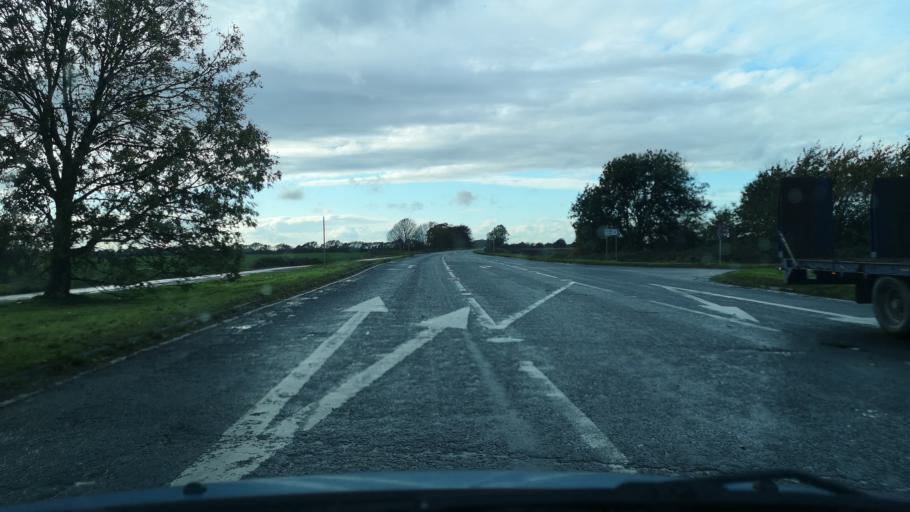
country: GB
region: England
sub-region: North Lincolnshire
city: Crowle
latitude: 53.5803
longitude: -0.8830
